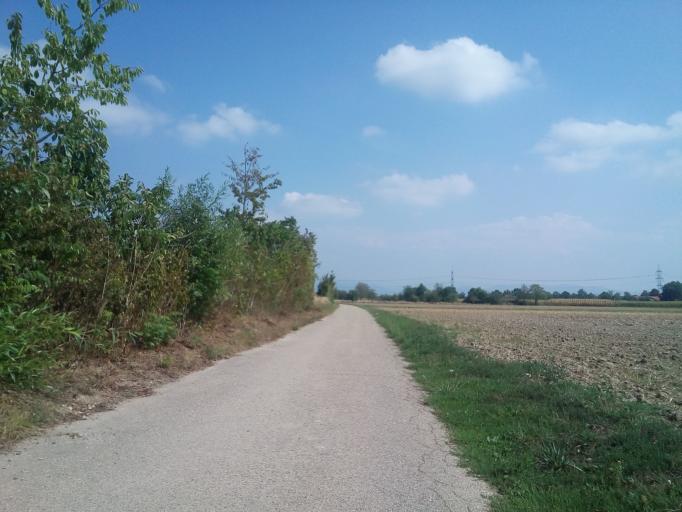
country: DE
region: Baden-Wuerttemberg
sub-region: Freiburg Region
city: Rheinau
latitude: 48.6330
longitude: 7.9147
